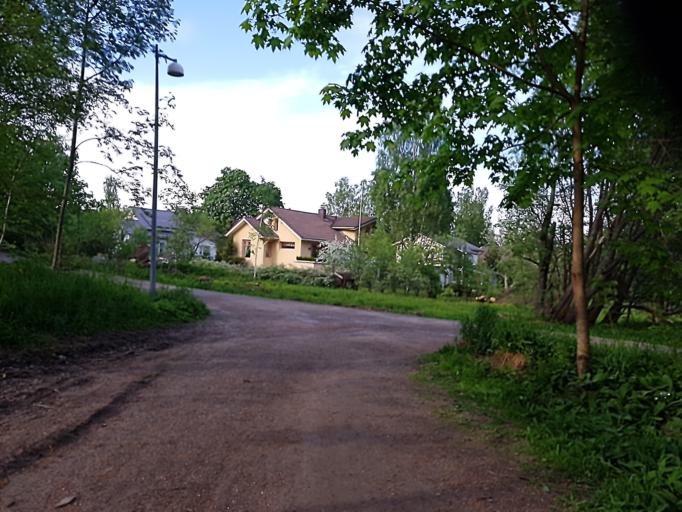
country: FI
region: Uusimaa
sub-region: Helsinki
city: Helsinki
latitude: 60.2360
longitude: 24.9386
